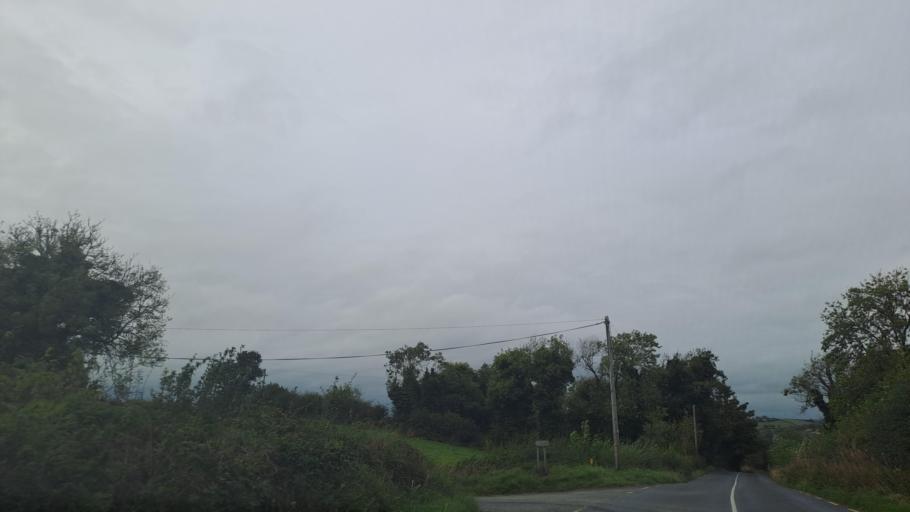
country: IE
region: Ulster
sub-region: An Cabhan
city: Bailieborough
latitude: 53.9855
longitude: -6.8840
